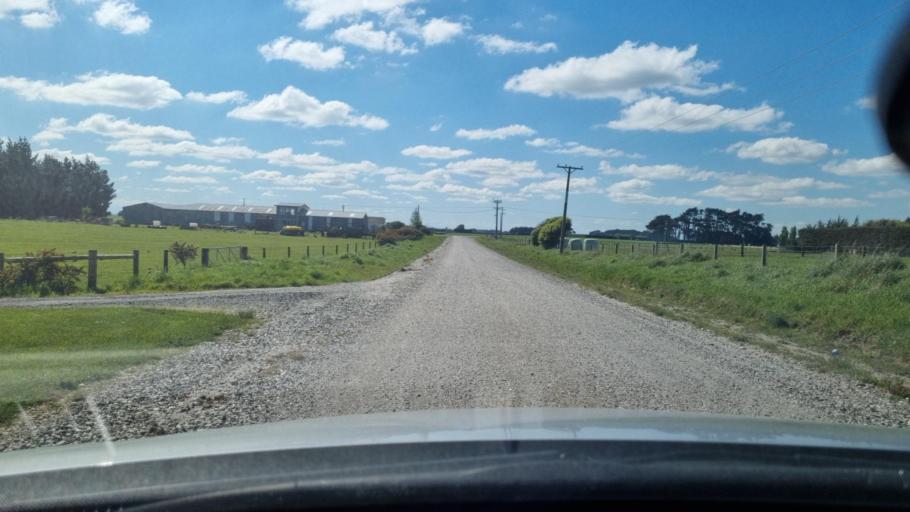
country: NZ
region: Southland
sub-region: Invercargill City
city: Invercargill
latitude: -46.3714
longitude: 168.2985
